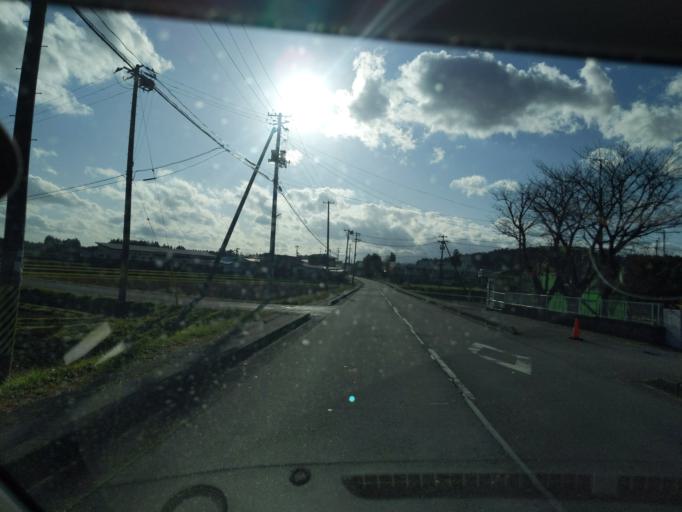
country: JP
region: Iwate
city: Mizusawa
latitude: 39.1223
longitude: 141.1127
